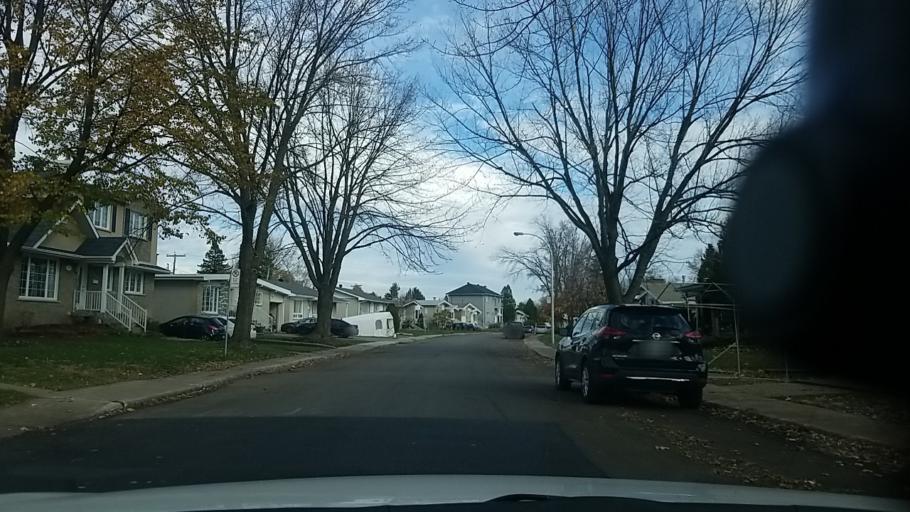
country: CA
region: Quebec
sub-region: Laval
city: Laval
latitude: 45.5744
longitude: -73.7355
